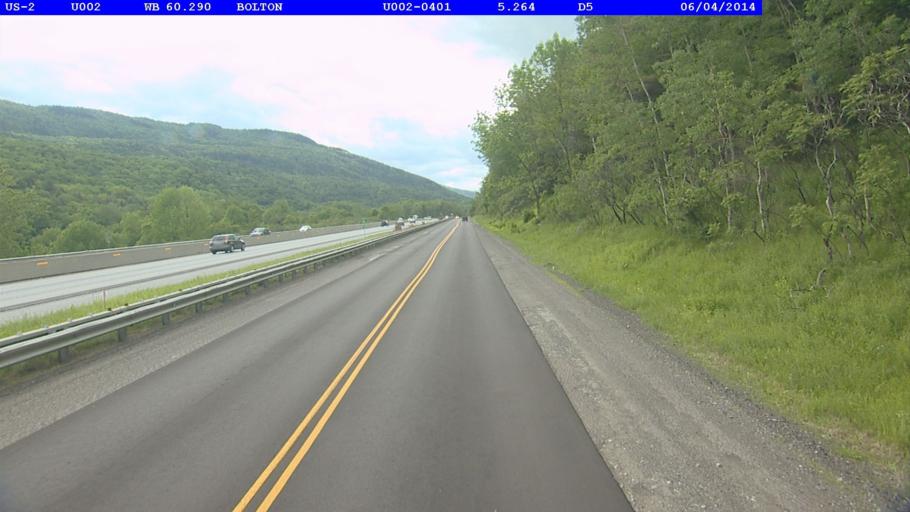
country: US
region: Vermont
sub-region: Washington County
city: Waterbury
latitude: 44.3619
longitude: -72.8327
